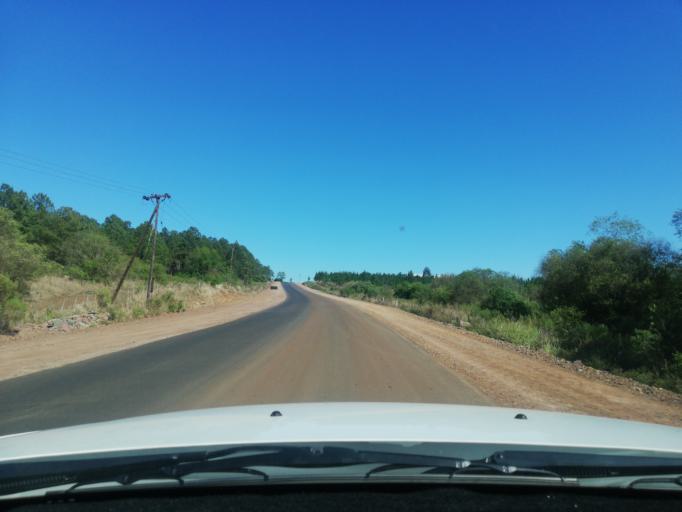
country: AR
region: Misiones
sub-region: Departamento de Candelaria
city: Candelaria
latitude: -27.5139
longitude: -55.7326
